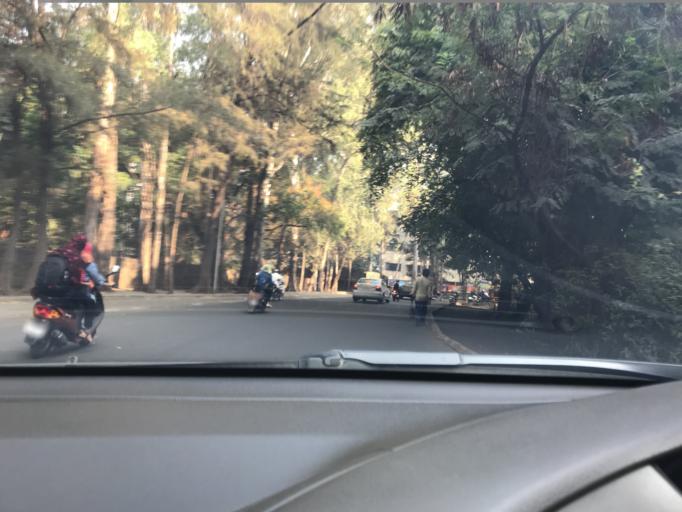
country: IN
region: Maharashtra
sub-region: Pune Division
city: Pune
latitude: 18.5092
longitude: 73.8286
